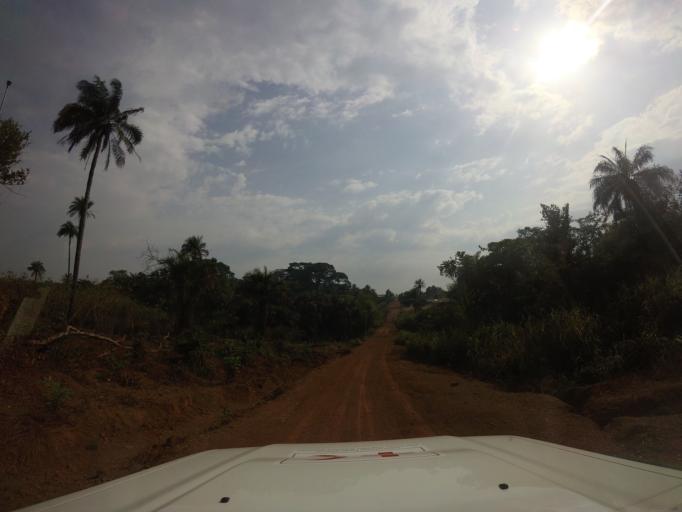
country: LR
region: Grand Cape Mount
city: Robertsport
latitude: 7.0026
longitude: -11.2923
